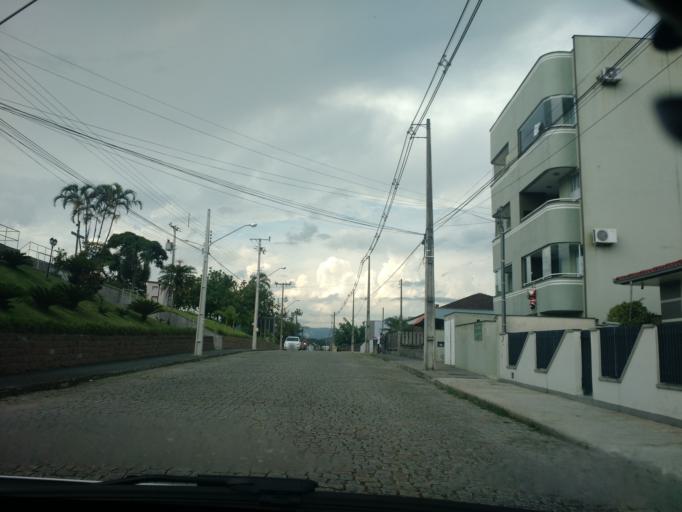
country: BR
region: Santa Catarina
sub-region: Jaragua Do Sul
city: Jaragua do Sul
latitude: -26.4792
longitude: -49.1071
